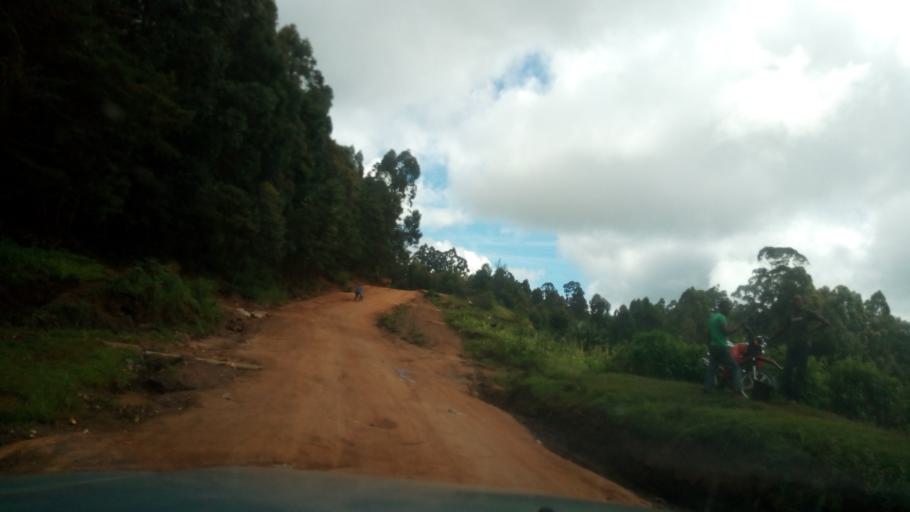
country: KE
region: Makueni
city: Wote
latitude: -1.6670
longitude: 37.4499
